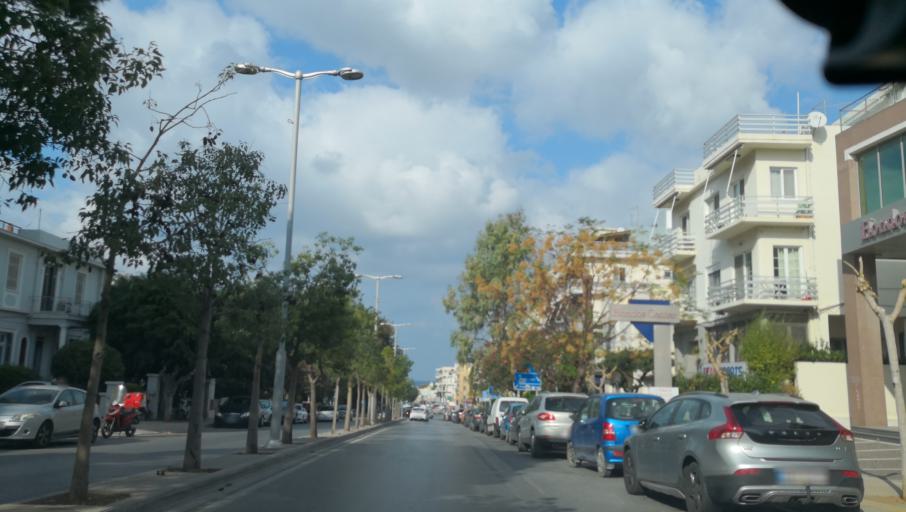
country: GR
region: Crete
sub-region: Nomos Irakleiou
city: Irakleion
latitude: 35.3339
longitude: 25.1386
